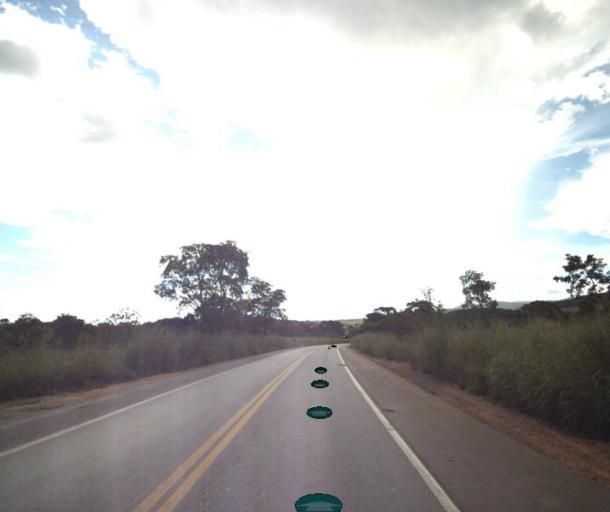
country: BR
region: Goias
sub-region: Jaragua
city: Jaragua
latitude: -15.6573
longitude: -49.3602
